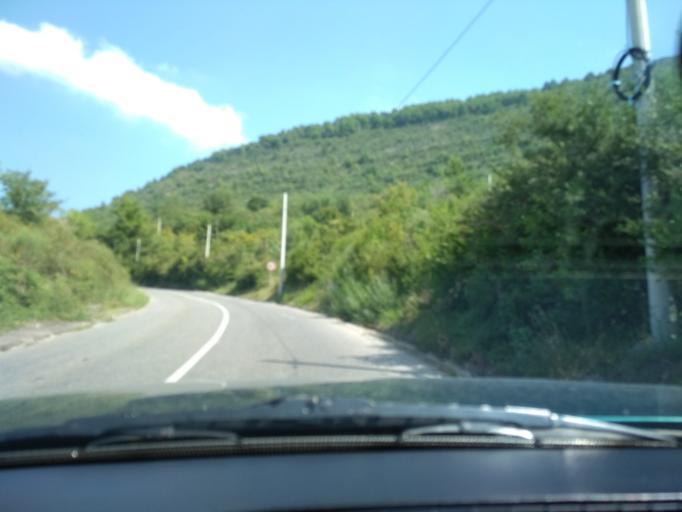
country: ME
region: Kotor
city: Kotor
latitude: 42.3883
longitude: 18.7577
